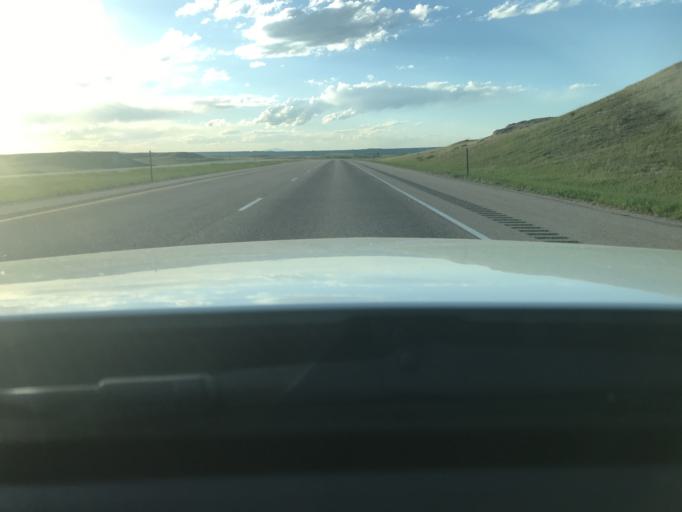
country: US
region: Wyoming
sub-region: Platte County
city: Wheatland
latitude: 41.7052
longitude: -104.8330
